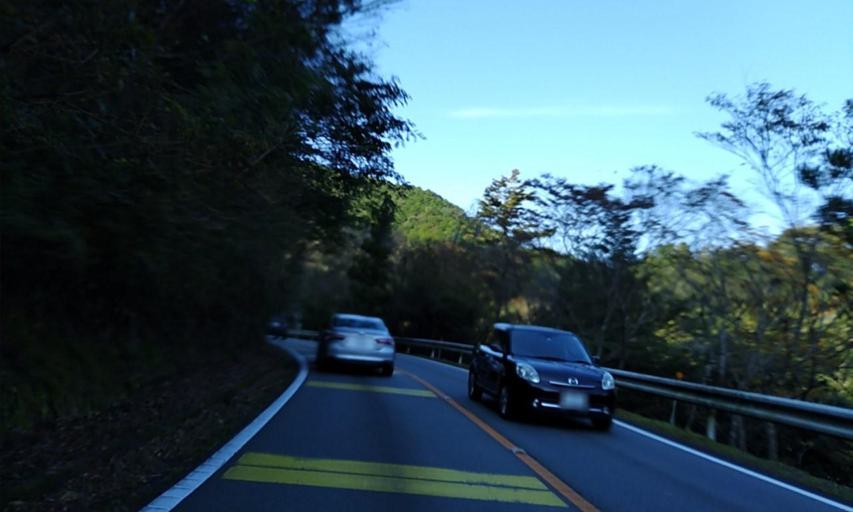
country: JP
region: Mie
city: Ise
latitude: 34.4511
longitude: 136.7468
